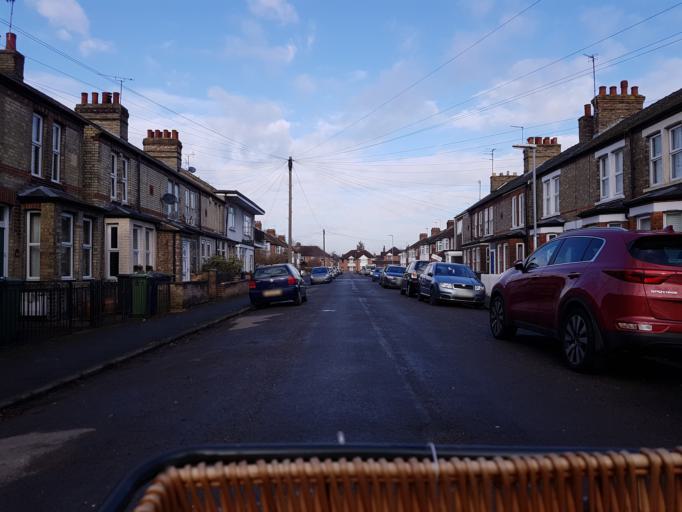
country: GB
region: England
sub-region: Cambridgeshire
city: Cambridge
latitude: 52.1886
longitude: 0.1483
